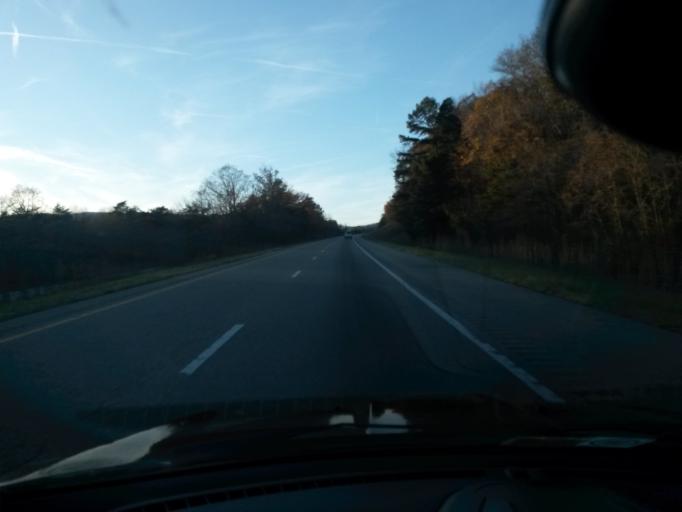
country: US
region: Virginia
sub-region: City of Lexington
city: Lexington
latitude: 37.8783
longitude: -79.5386
